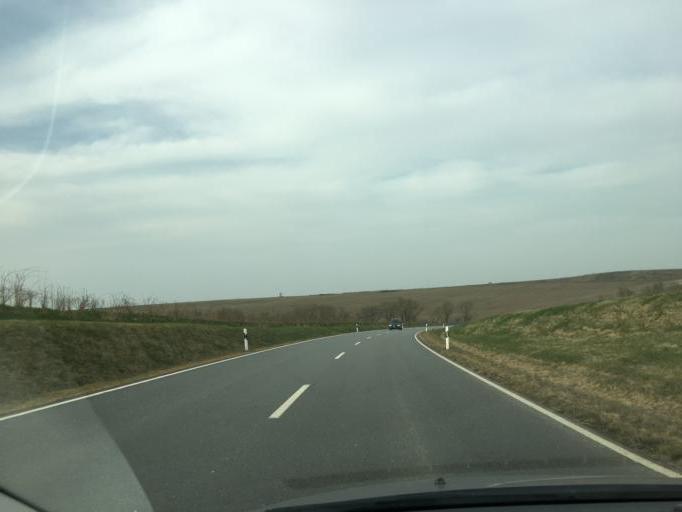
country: DE
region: Saxony
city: Niederfrohna
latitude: 50.8991
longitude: 12.7159
